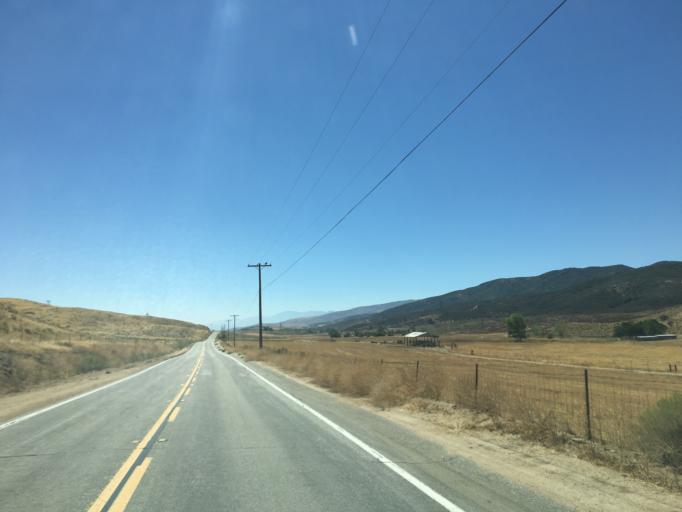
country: US
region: California
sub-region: Los Angeles County
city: Green Valley
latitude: 34.6420
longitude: -118.3594
